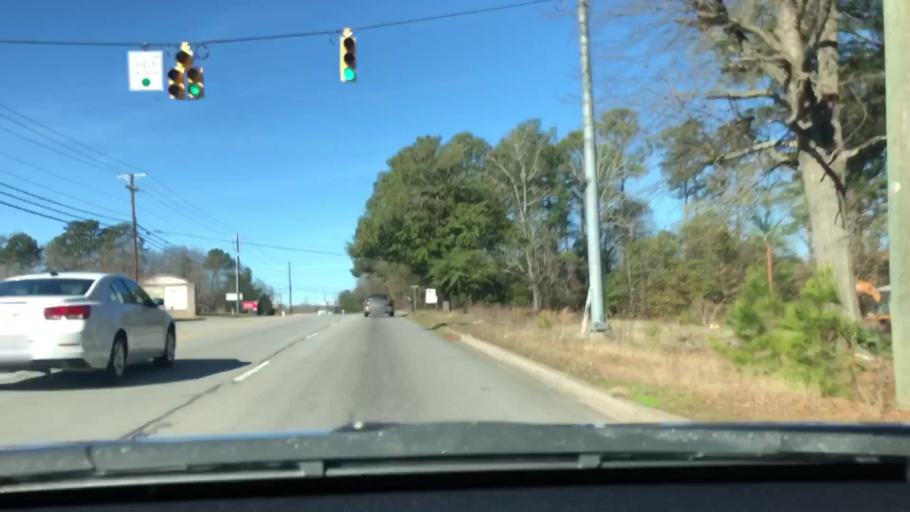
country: US
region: South Carolina
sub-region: Lexington County
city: Oak Grove
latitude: 34.0070
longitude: -81.1234
